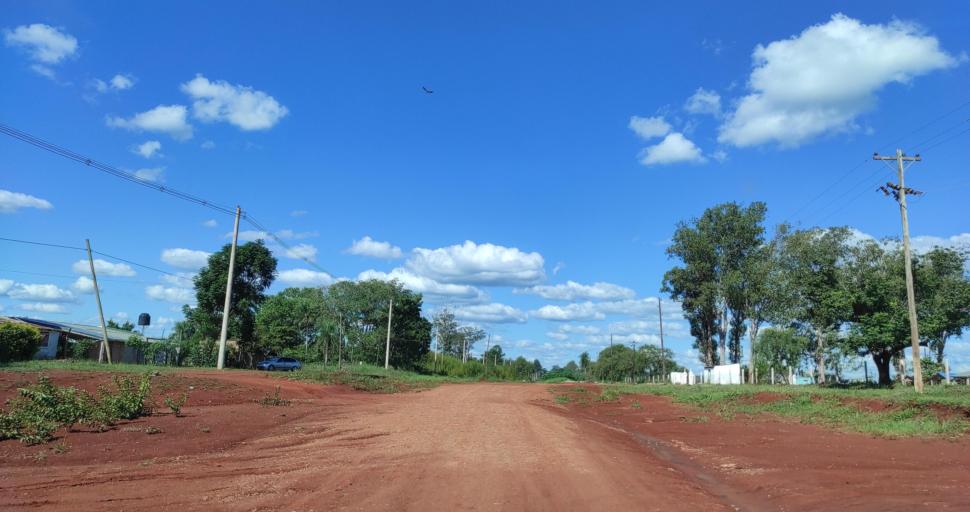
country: AR
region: Misiones
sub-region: Departamento de Candelaria
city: Candelaria
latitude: -27.4637
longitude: -55.7241
